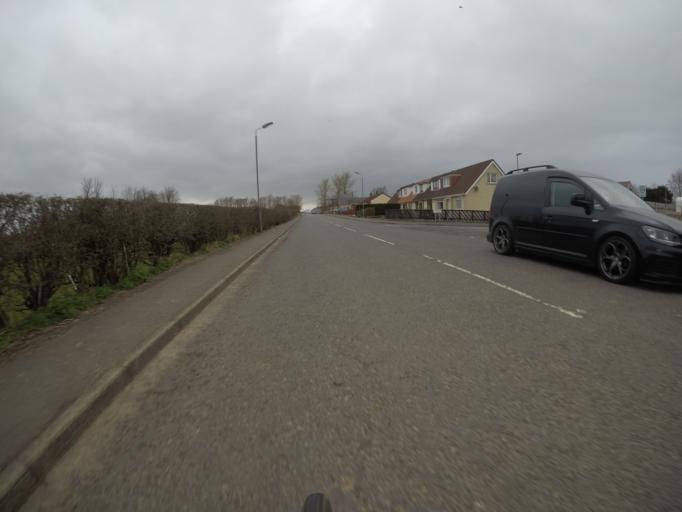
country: GB
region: Scotland
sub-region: North Ayrshire
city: Springside
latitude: 55.6166
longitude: -4.5902
